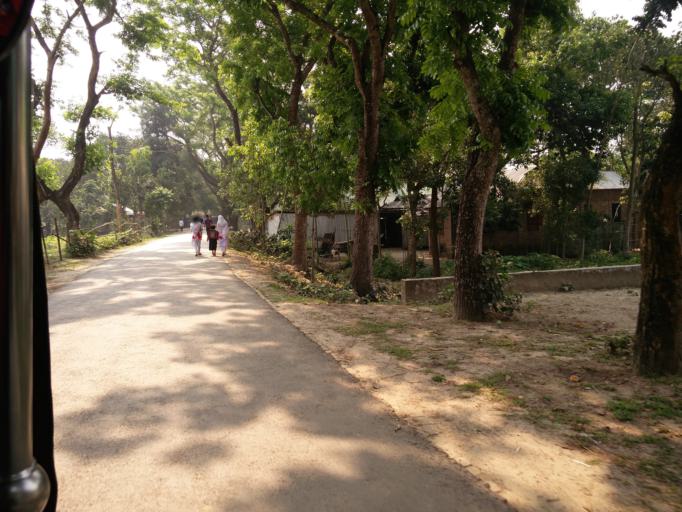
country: BD
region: Dhaka
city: Muktagacha
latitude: 24.9082
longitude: 90.2085
